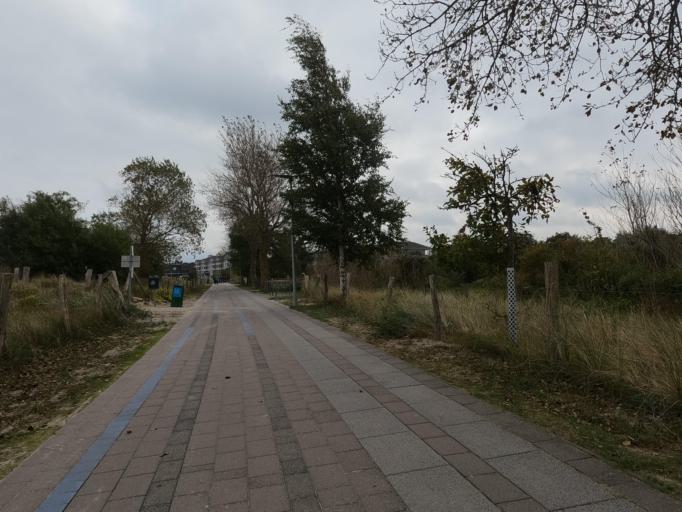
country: DE
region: Schleswig-Holstein
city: Heiligenhafen
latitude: 54.3809
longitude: 10.9738
